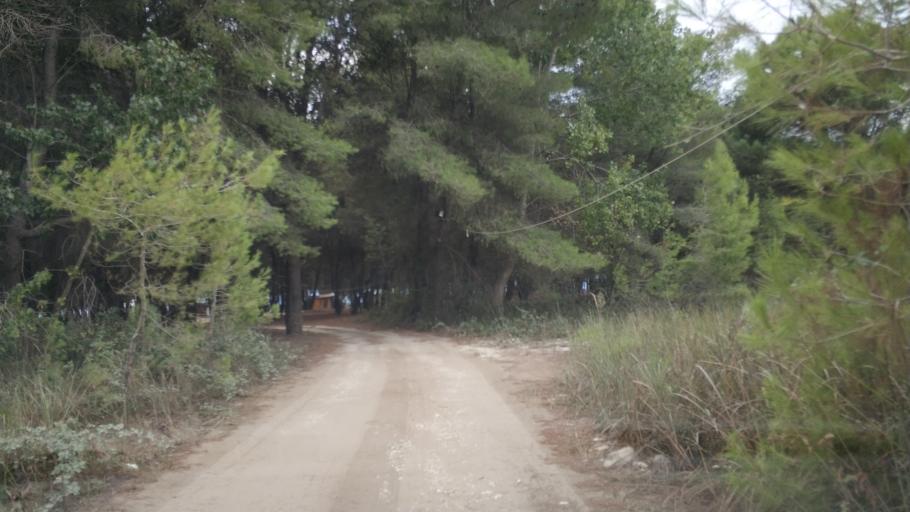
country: AL
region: Vlore
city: Vlore
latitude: 40.5027
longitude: 19.4198
